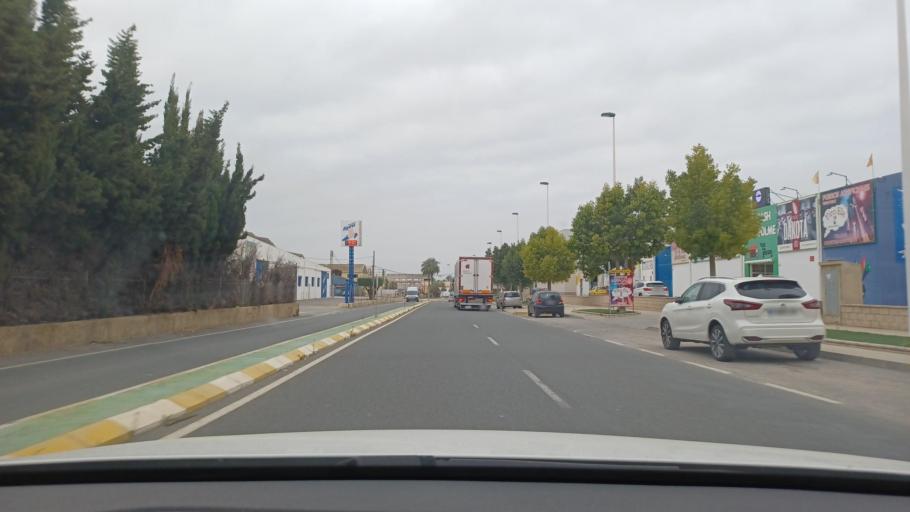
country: ES
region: Valencia
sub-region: Provincia de Alicante
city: Elche
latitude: 38.2464
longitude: -0.7057
